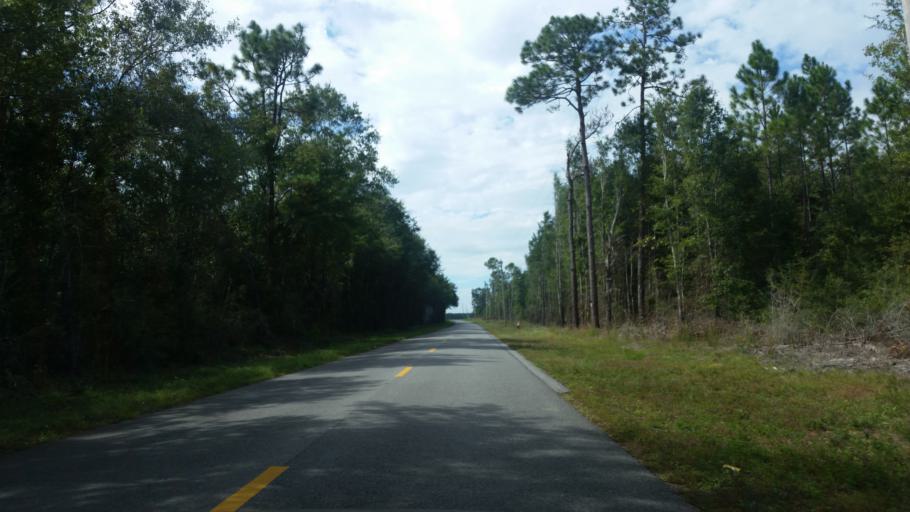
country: US
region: Florida
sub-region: Santa Rosa County
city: Point Baker
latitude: 30.7364
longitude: -87.0172
